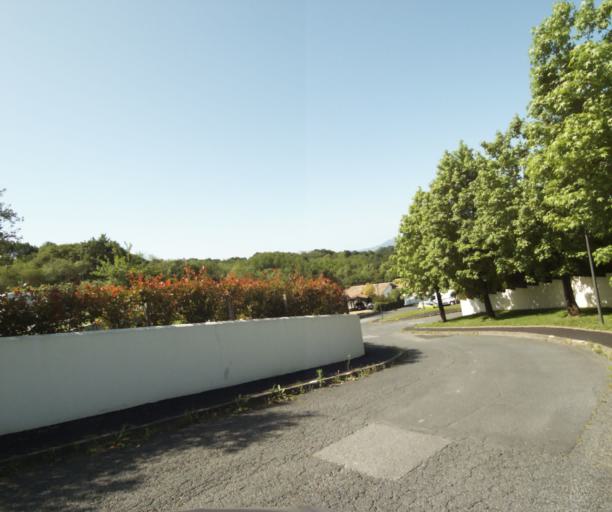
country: FR
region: Aquitaine
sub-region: Departement des Pyrenees-Atlantiques
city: Villefranque
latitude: 43.4574
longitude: -1.4498
